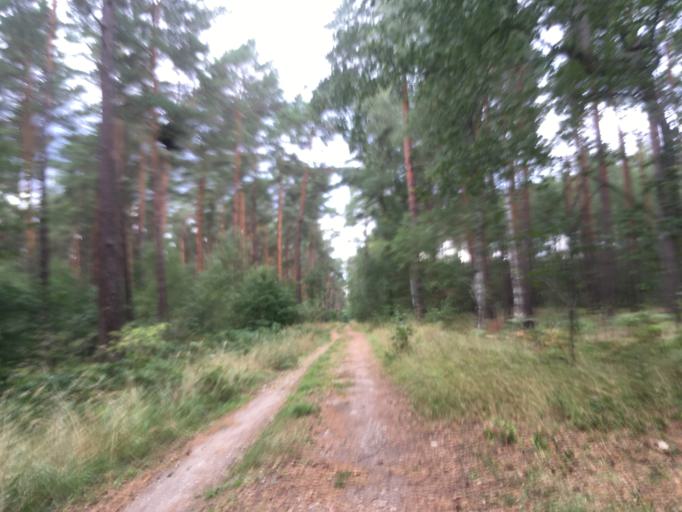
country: DE
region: Brandenburg
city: Wildau
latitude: 52.3277
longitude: 13.7005
